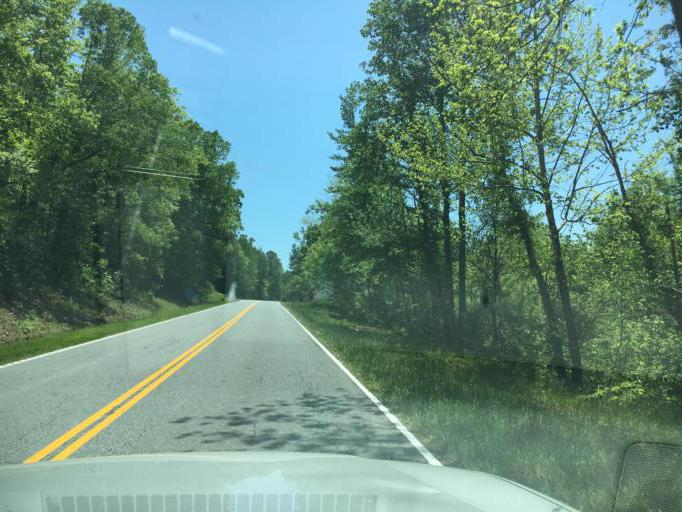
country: US
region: South Carolina
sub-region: Cherokee County
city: Blacksburg
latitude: 35.1316
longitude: -81.5833
